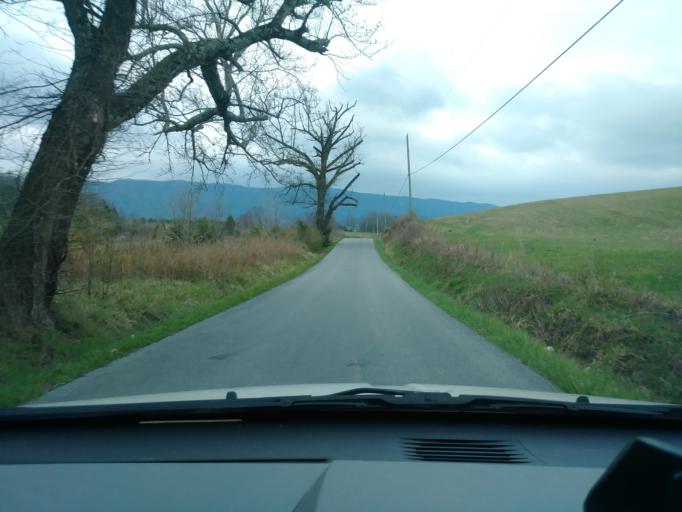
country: US
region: Tennessee
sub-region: Greene County
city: Tusculum
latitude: 36.0942
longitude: -82.7505
